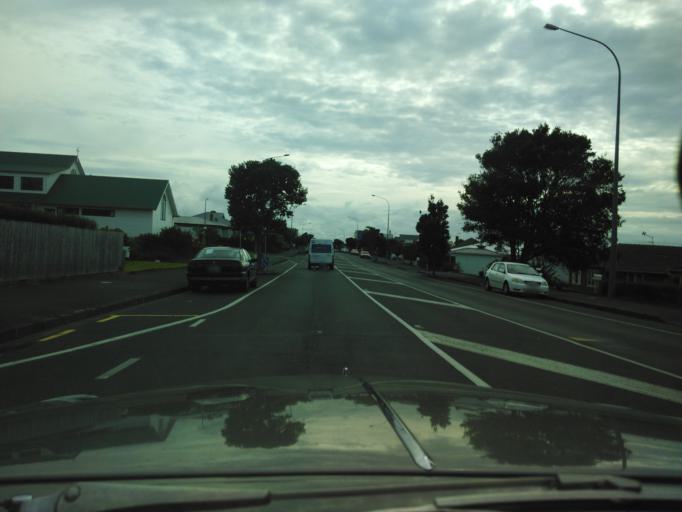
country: NZ
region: Auckland
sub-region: Auckland
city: Rosebank
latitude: -36.8676
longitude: 174.7081
